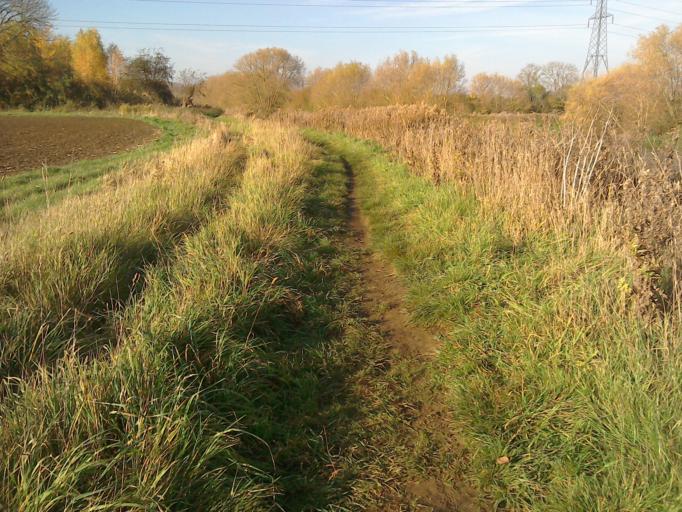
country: GB
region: England
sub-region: Oxfordshire
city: Radley
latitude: 51.6939
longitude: -1.2258
